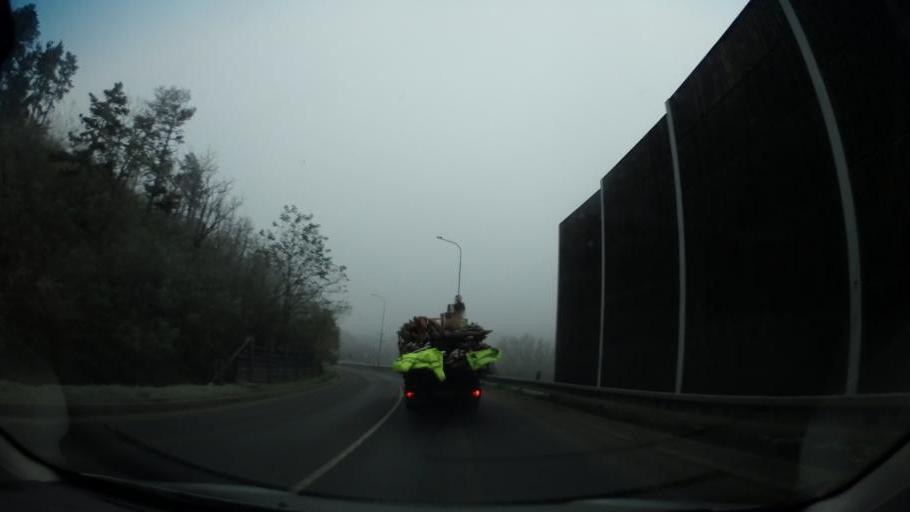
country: CZ
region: Vysocina
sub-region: Okres Trebic
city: Trebic
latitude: 49.2175
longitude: 15.9003
